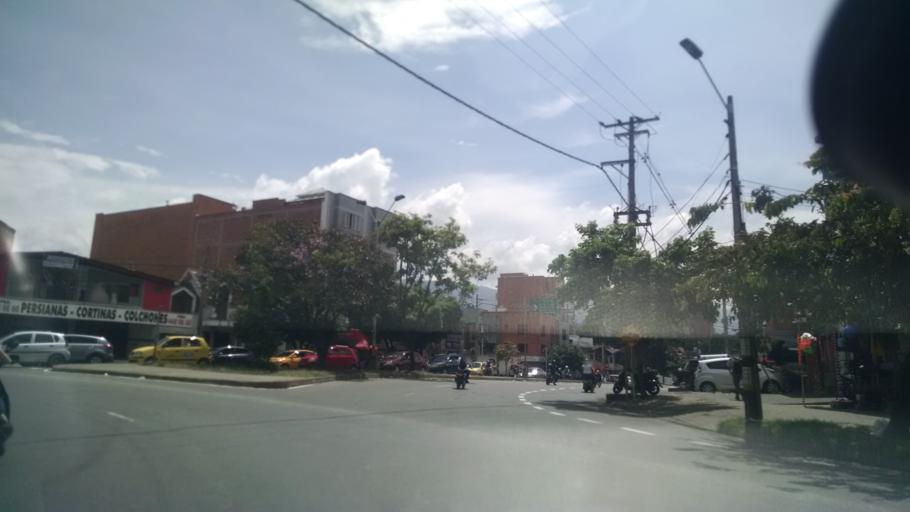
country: CO
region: Antioquia
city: Medellin
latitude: 6.2633
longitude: -75.5967
